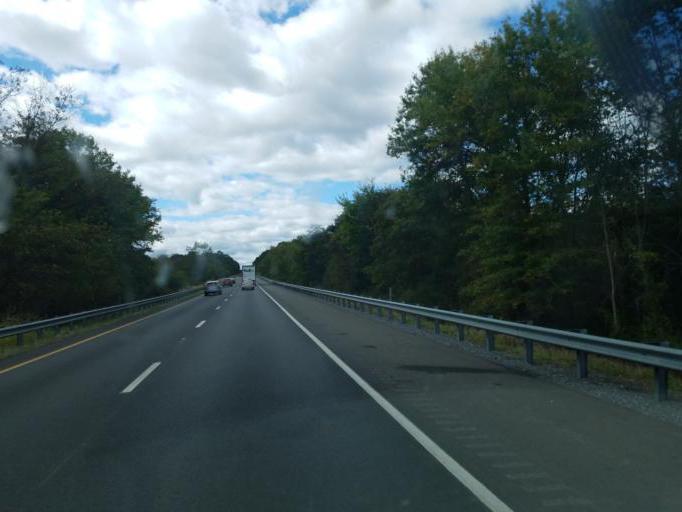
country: US
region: Maryland
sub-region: Washington County
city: Wilson-Conococheague
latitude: 39.6284
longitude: -77.9758
